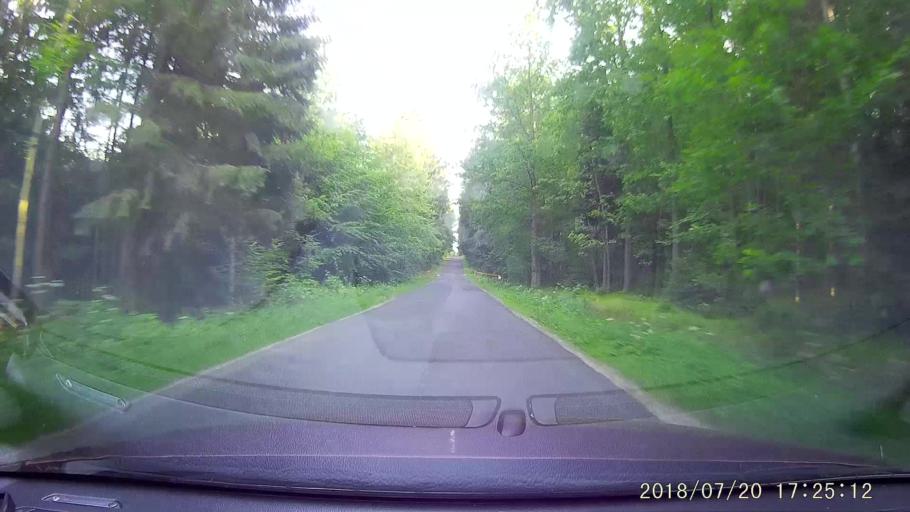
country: PL
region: Lower Silesian Voivodeship
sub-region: Powiat lubanski
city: Swieradow-Zdroj
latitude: 50.9635
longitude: 15.2997
